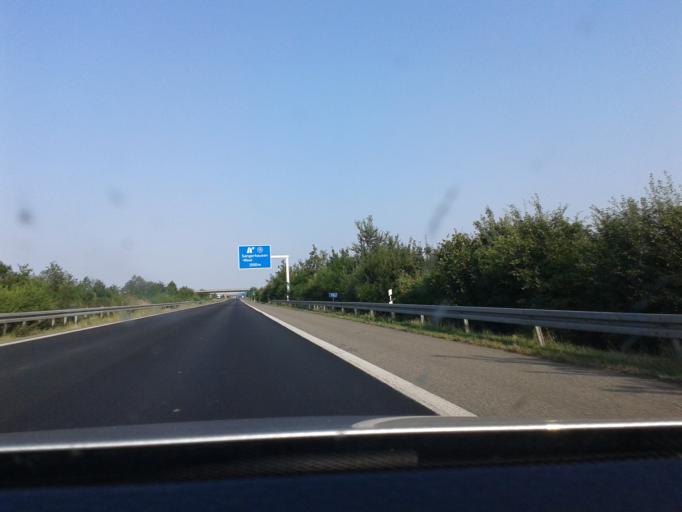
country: DE
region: Saxony-Anhalt
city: Wallhausen
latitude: 51.4504
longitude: 11.2429
